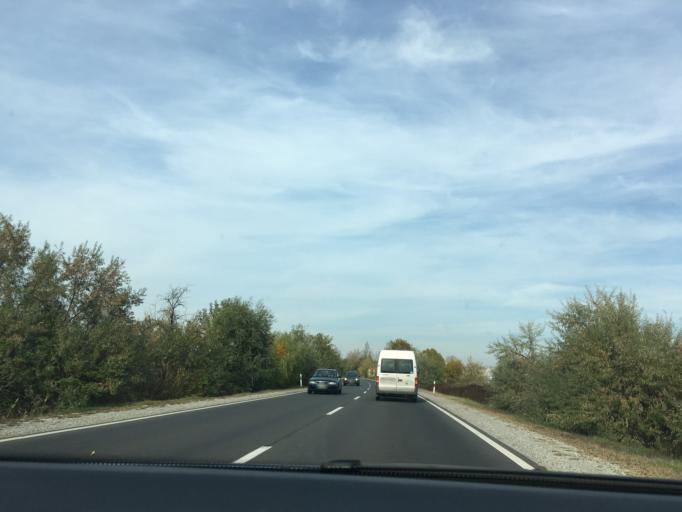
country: HU
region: Szabolcs-Szatmar-Bereg
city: Ujfeherto
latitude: 47.8030
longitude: 21.7041
